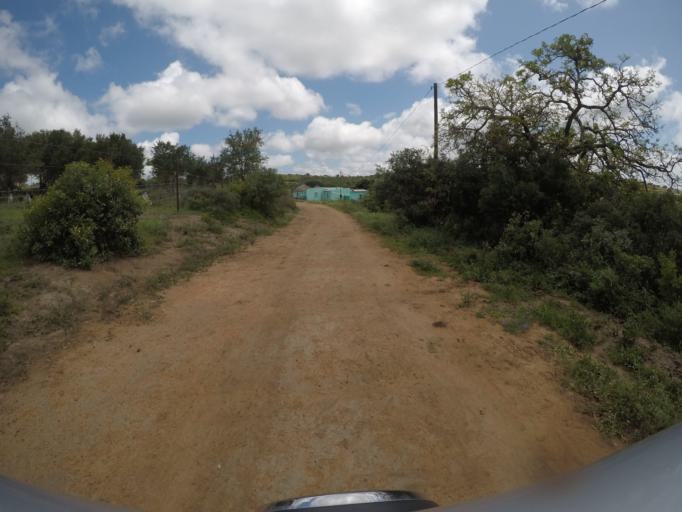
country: ZA
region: KwaZulu-Natal
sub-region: uThungulu District Municipality
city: Empangeni
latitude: -28.5837
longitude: 31.8328
